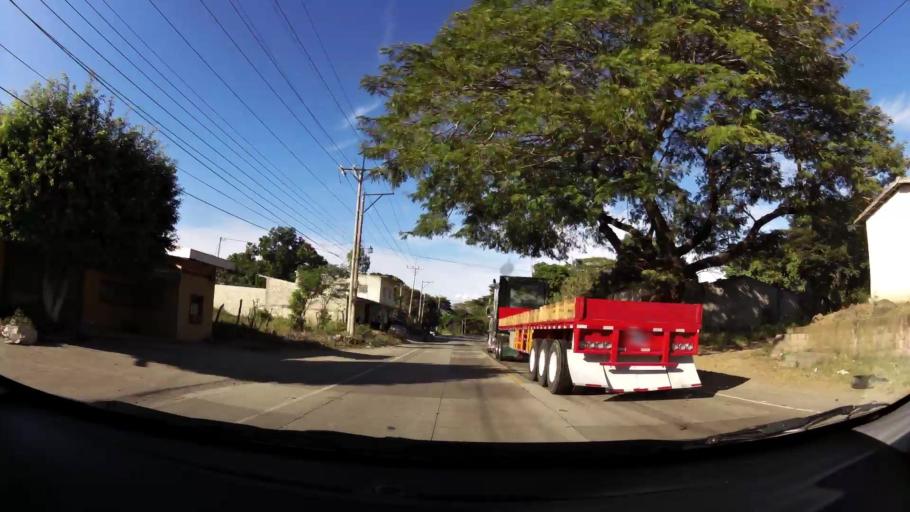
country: SV
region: Santa Ana
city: Metapan
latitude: 14.2981
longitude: -89.4631
